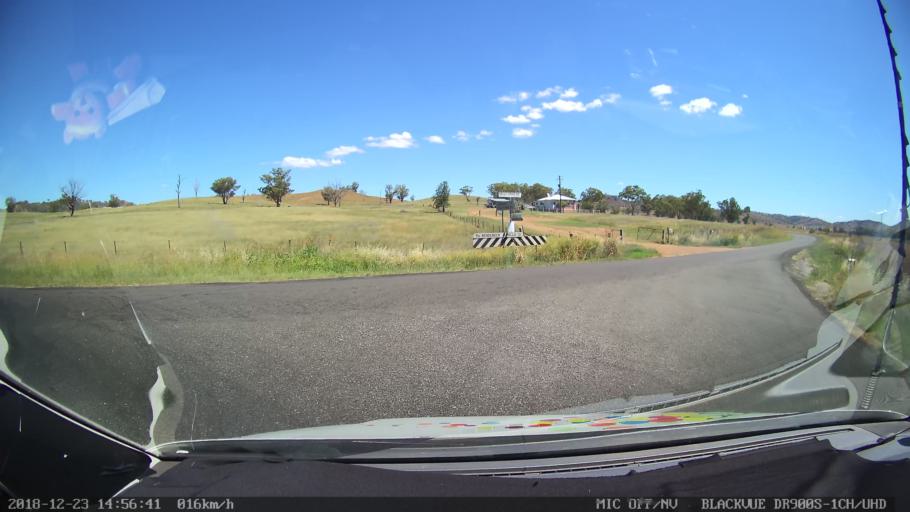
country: AU
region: New South Wales
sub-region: Tamworth Municipality
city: Manilla
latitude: -30.7051
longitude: 150.8294
